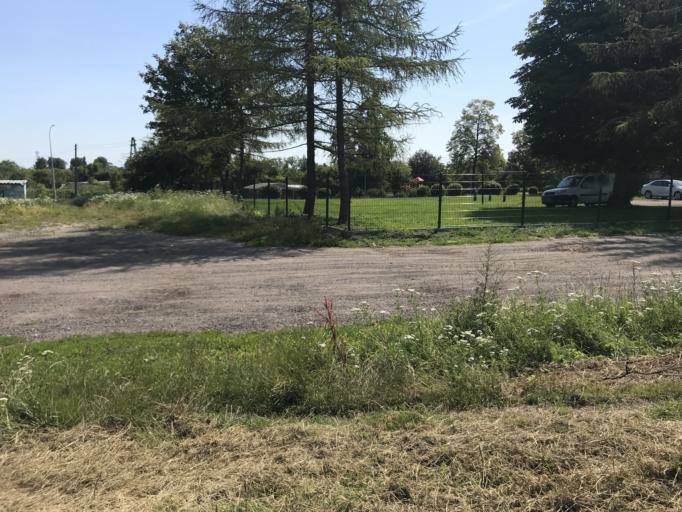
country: PL
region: Pomeranian Voivodeship
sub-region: Gdansk
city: Gdansk
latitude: 54.3417
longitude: 18.6684
